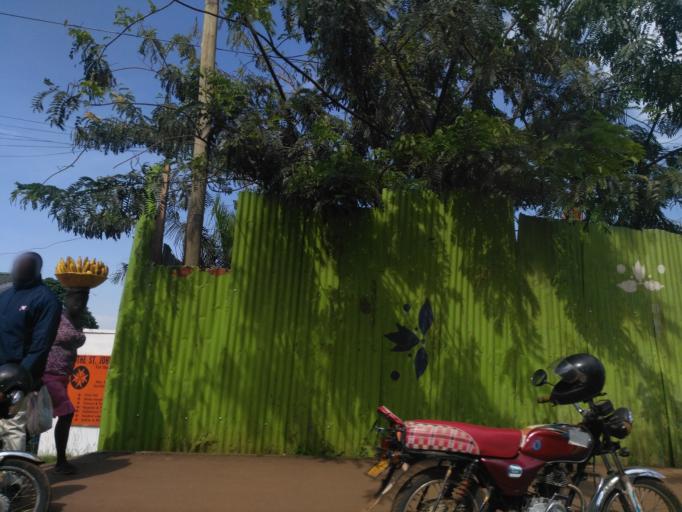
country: UG
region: Central Region
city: Kampala Central Division
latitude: 0.3267
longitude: 32.5750
